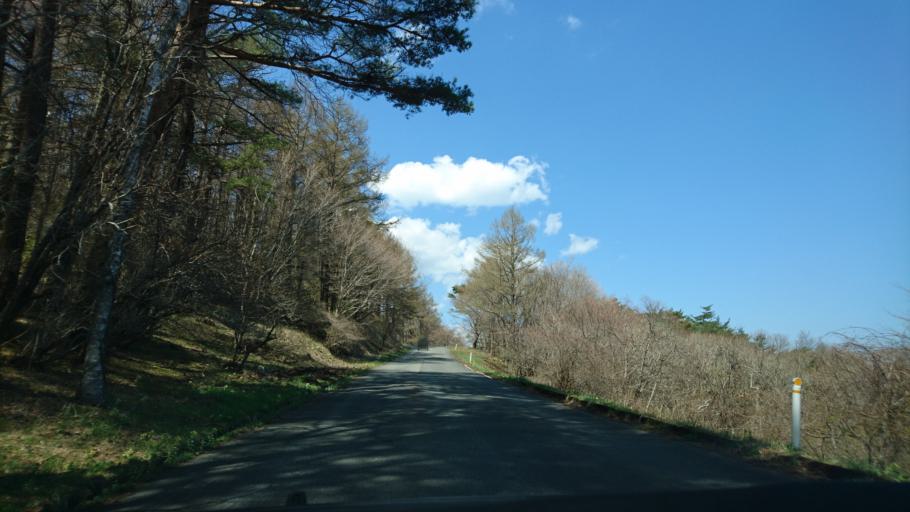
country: JP
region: Iwate
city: Ofunato
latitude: 38.9737
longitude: 141.4573
